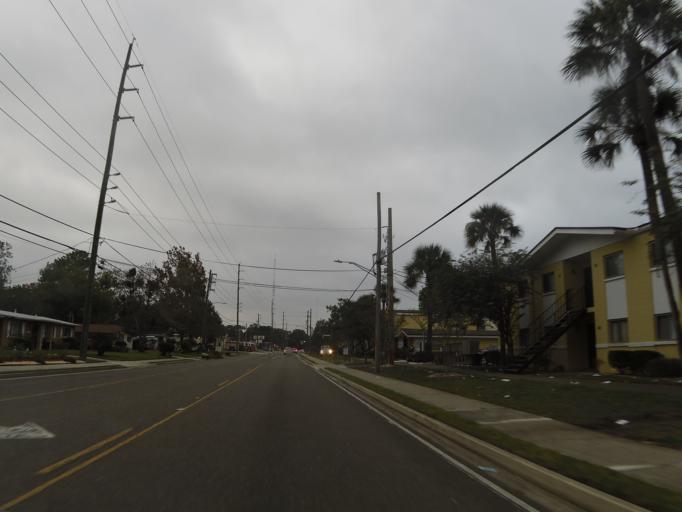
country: US
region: Florida
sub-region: Clay County
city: Bellair-Meadowbrook Terrace
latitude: 30.2797
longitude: -81.7478
